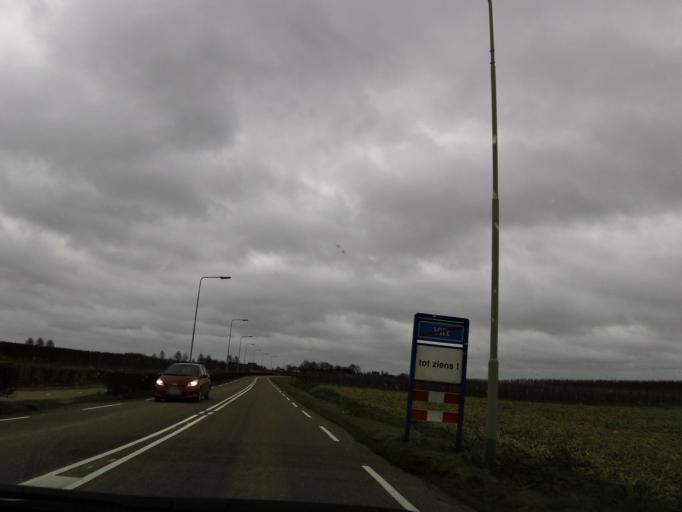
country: NL
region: Limburg
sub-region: Valkenburg aan de Geul
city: Sibbe
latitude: 50.8535
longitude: 5.8126
